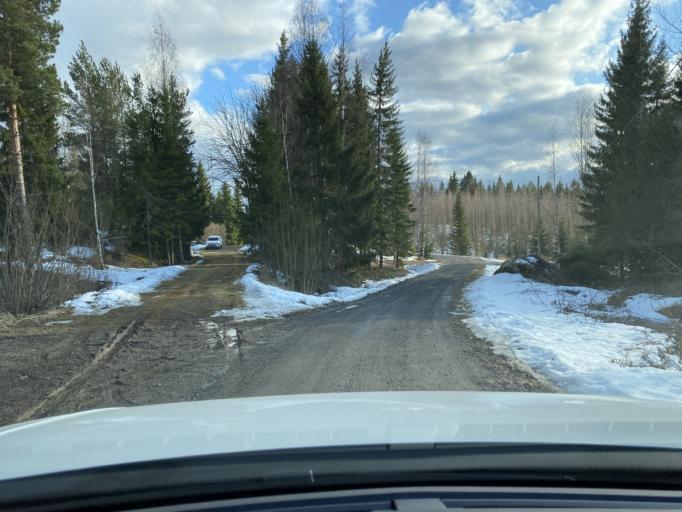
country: FI
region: Pirkanmaa
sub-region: Lounais-Pirkanmaa
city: Mouhijaervi
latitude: 61.4467
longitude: 22.9606
